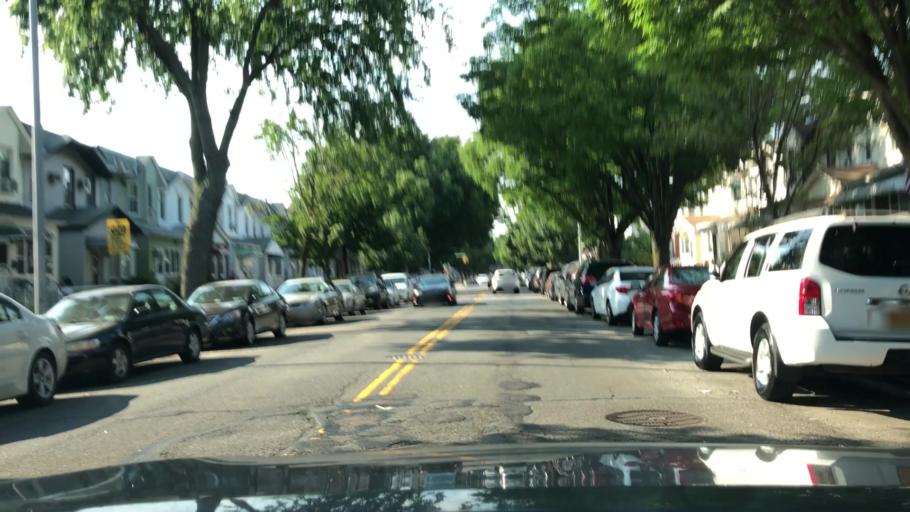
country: US
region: New York
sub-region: Queens County
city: Borough of Queens
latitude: 40.6813
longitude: -73.8294
